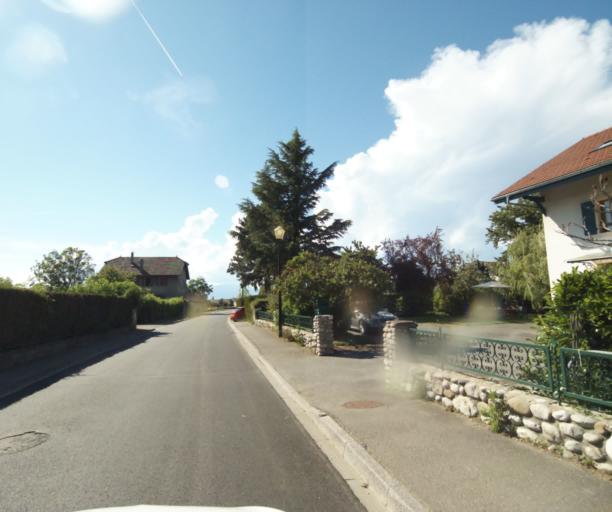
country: FR
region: Rhone-Alpes
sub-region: Departement de la Haute-Savoie
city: Massongy
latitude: 46.3202
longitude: 6.3275
